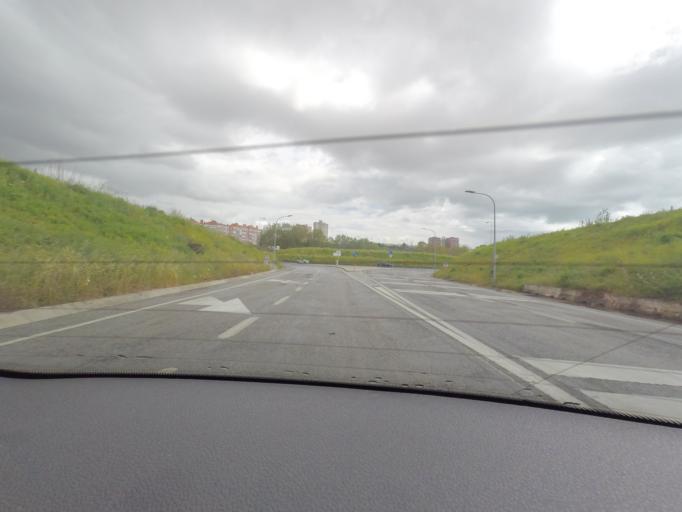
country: PT
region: Lisbon
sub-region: Cascais
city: Sao Domingos de Rana
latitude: 38.6969
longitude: -9.3343
